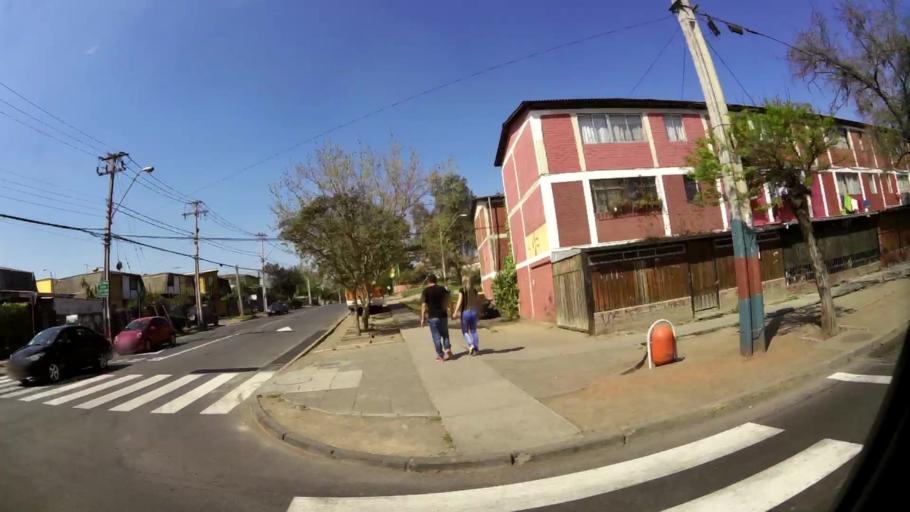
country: CL
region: Santiago Metropolitan
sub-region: Provincia de Santiago
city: Lo Prado
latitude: -33.5028
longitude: -70.7756
